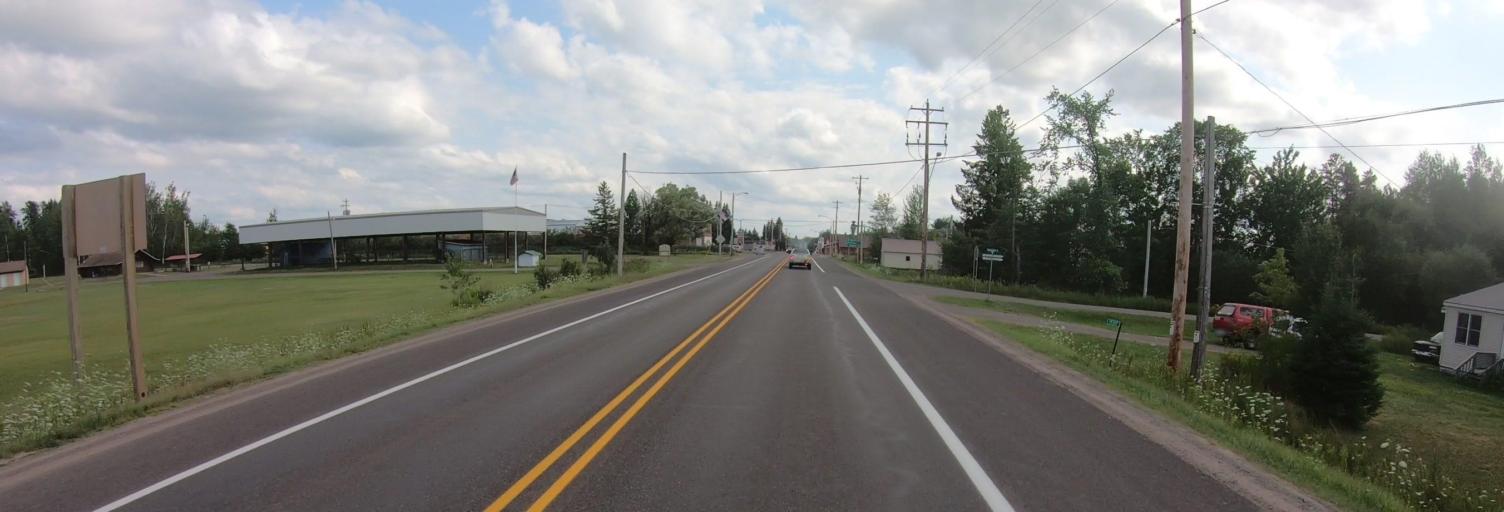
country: US
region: Michigan
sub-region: Ontonagon County
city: Ontonagon
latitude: 46.5374
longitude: -89.1785
